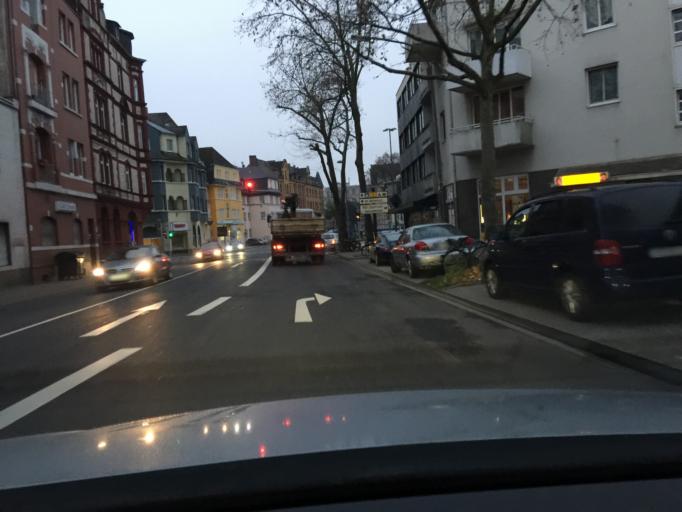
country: DE
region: Rheinland-Pfalz
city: Koblenz
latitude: 50.3672
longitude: 7.5946
